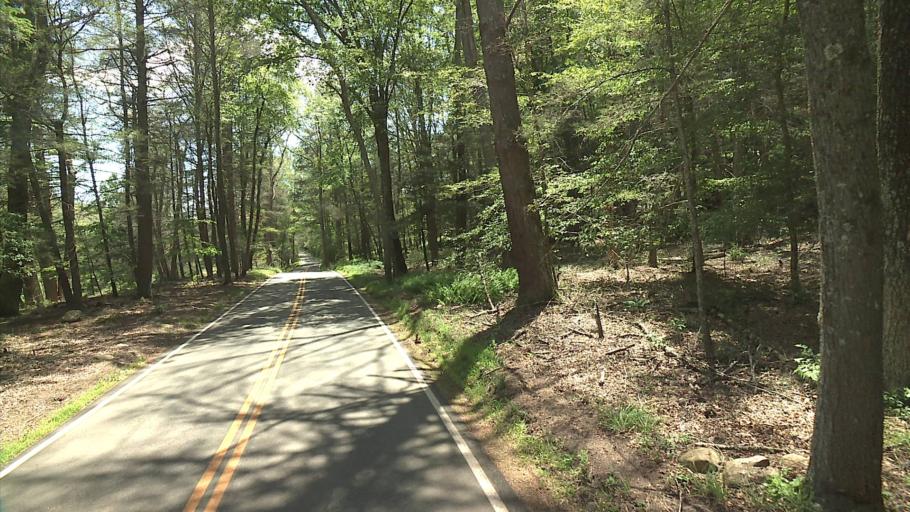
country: US
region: Connecticut
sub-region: New London County
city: Colchester
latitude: 41.4712
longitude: -72.3393
